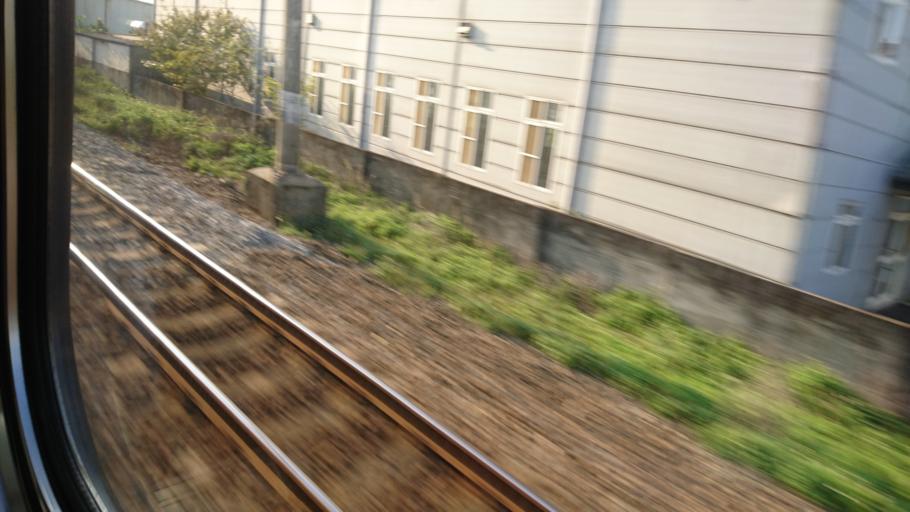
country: TW
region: Taiwan
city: Daxi
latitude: 24.9307
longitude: 121.1990
